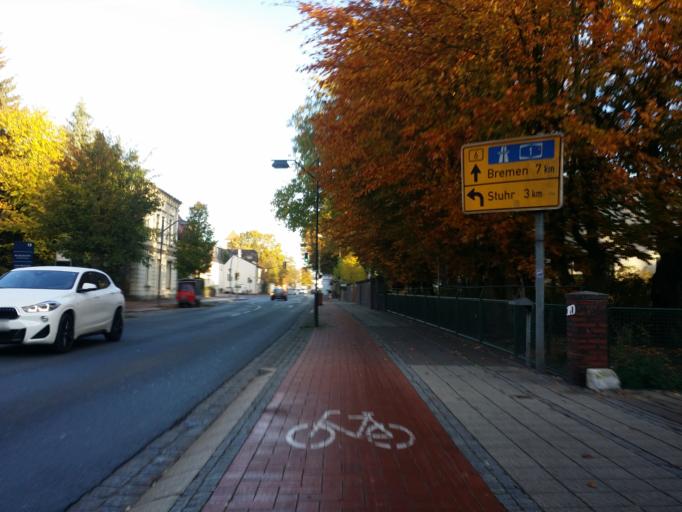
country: DE
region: Lower Saxony
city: Stuhr
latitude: 53.0131
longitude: 8.7893
